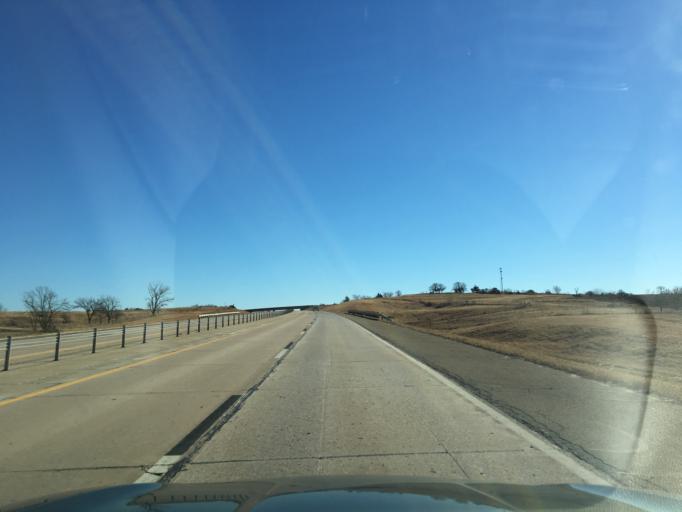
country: US
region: Oklahoma
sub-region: Payne County
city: Stillwater
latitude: 36.2505
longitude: -96.9662
